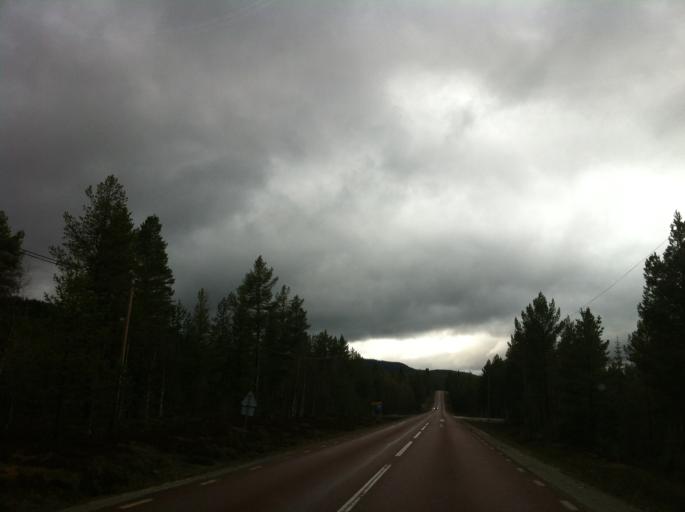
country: NO
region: Hedmark
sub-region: Engerdal
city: Engerdal
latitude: 62.4302
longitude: 12.7164
